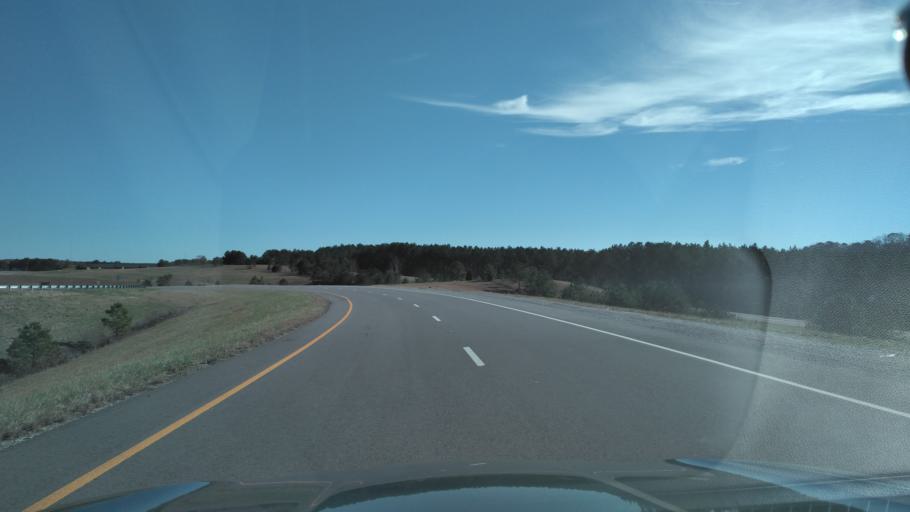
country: US
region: Alabama
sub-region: Walker County
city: Jasper
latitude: 33.8547
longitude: -87.3510
